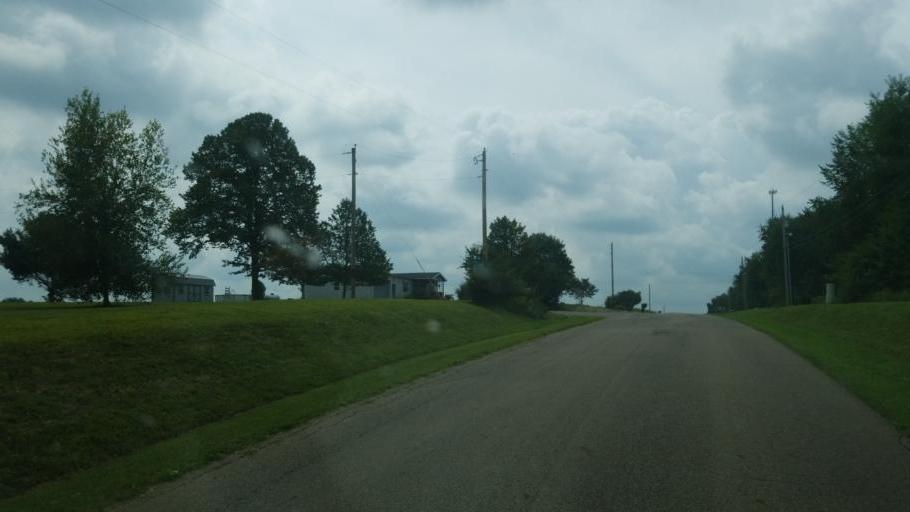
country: US
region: Ohio
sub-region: Knox County
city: Danville
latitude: 40.4496
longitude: -82.3276
